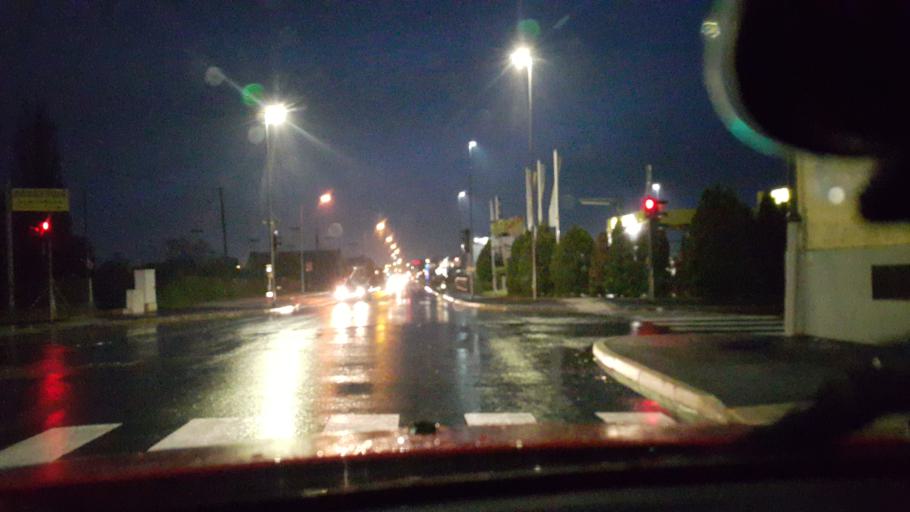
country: SI
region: Maribor
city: Maribor
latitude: 46.5350
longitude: 15.6575
